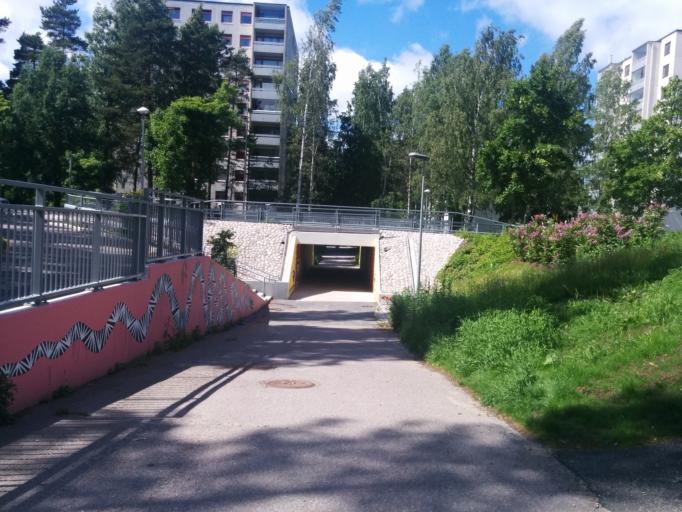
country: FI
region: Uusimaa
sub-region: Helsinki
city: Vantaa
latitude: 60.2441
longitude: 25.1170
